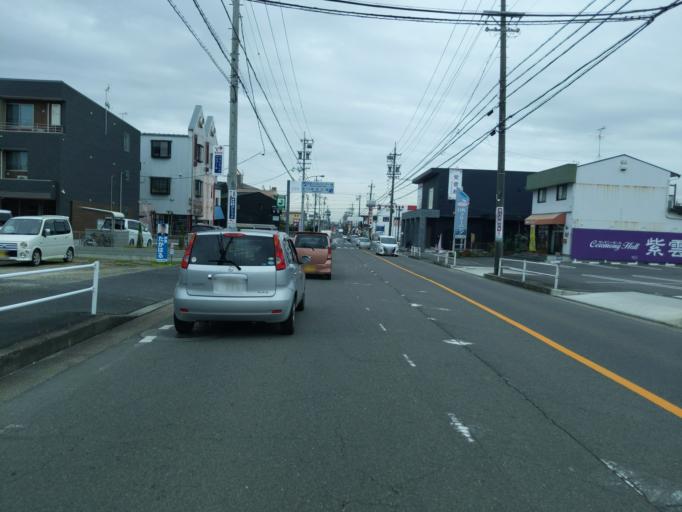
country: JP
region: Aichi
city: Kasugai
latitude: 35.2542
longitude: 136.9536
